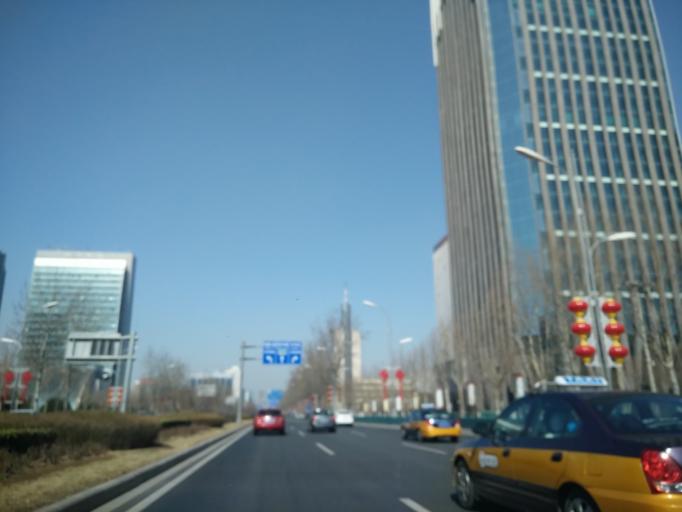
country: CN
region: Beijing
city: Jiugong
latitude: 39.7923
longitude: 116.5036
